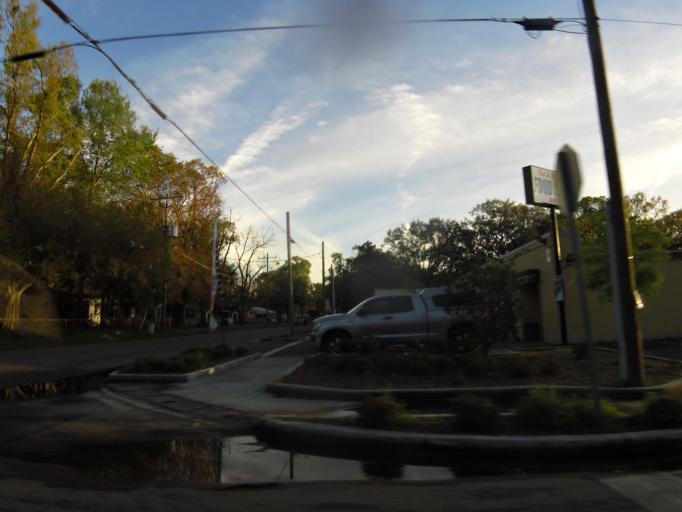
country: US
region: Florida
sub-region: Duval County
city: Jacksonville
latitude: 30.3402
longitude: -81.7141
